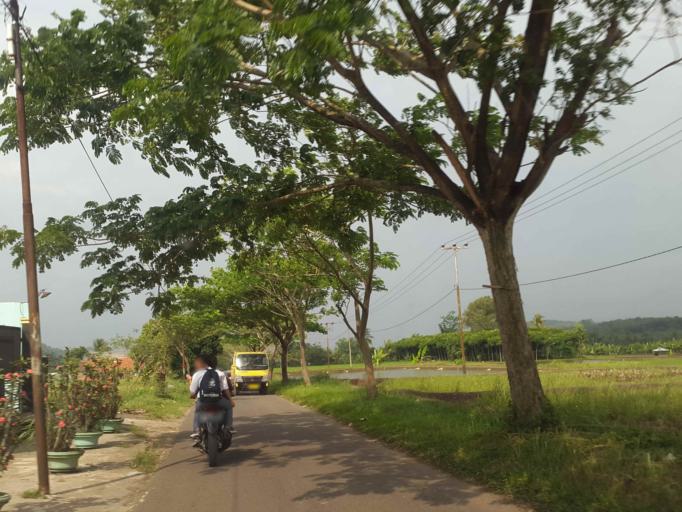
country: ID
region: West Java
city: Ciranjang-hilir
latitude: -6.7155
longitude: 107.2301
